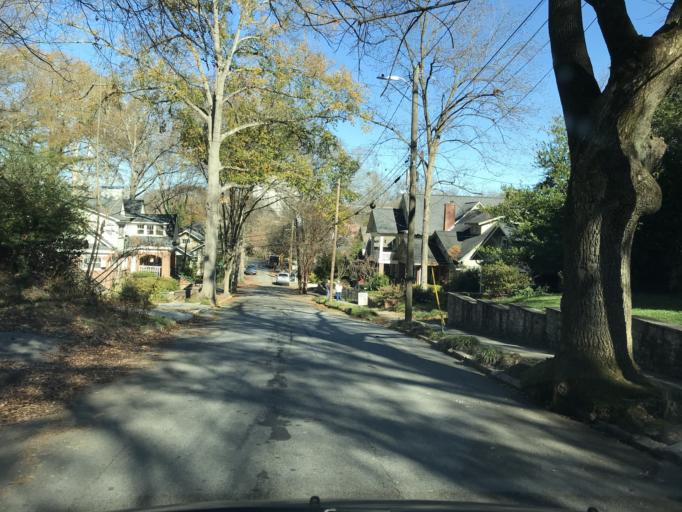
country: US
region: Georgia
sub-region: DeKalb County
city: Druid Hills
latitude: 33.7774
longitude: -84.3683
